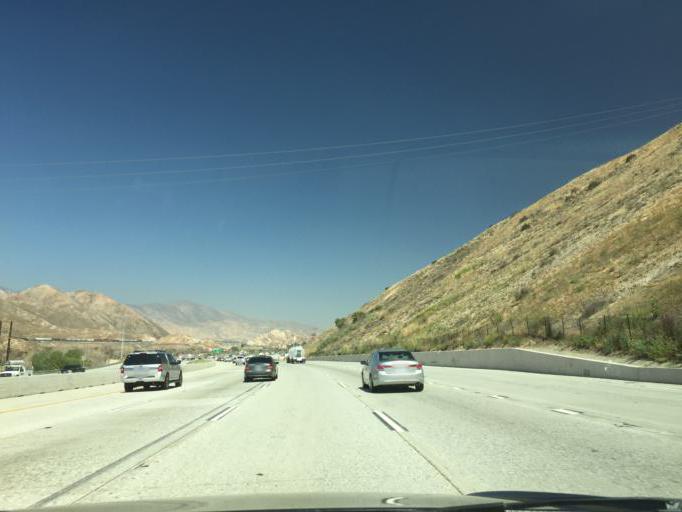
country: US
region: California
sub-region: San Bernardino County
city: Oak Hills
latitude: 34.3035
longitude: -117.4619
